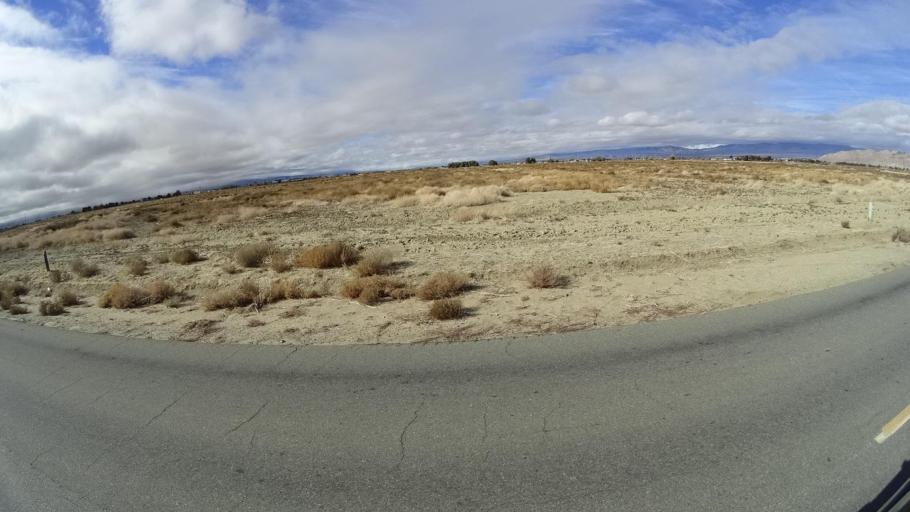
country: US
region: California
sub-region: Kern County
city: Rosamond
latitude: 34.8300
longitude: -118.2378
